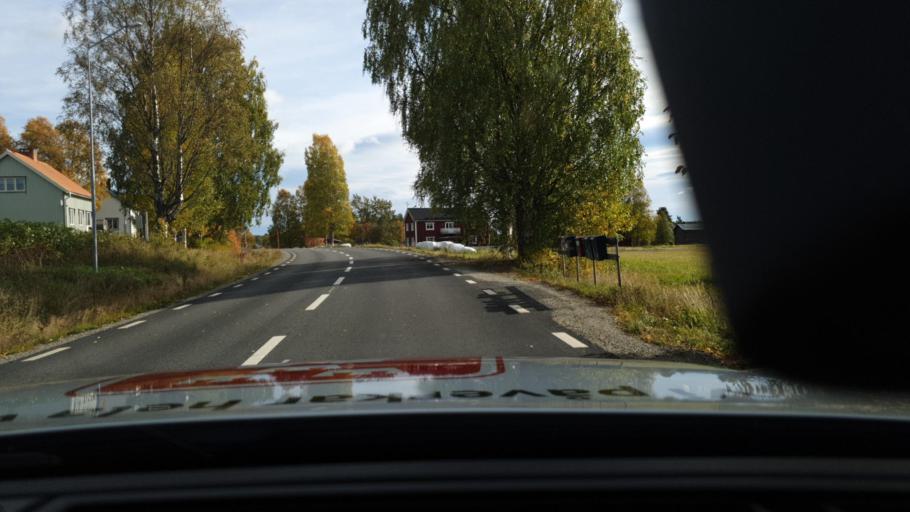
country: SE
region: Vaesterbotten
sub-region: Lycksele Kommun
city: Lycksele
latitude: 64.8154
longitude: 18.8868
